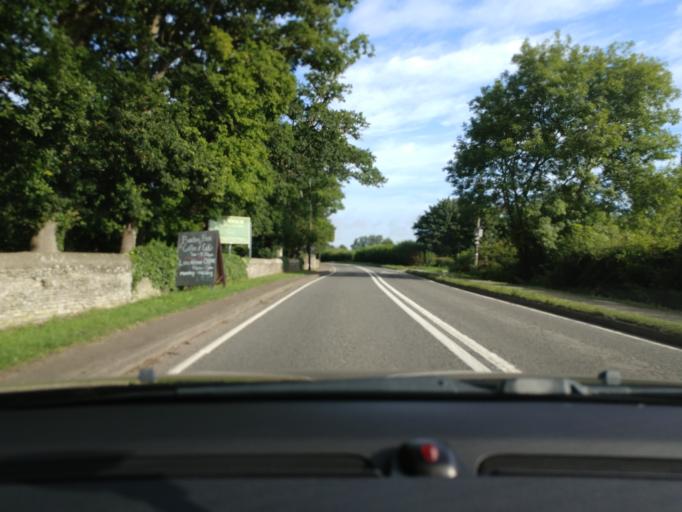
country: GB
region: England
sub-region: Oxfordshire
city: Kidlington
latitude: 51.8619
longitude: -1.2242
